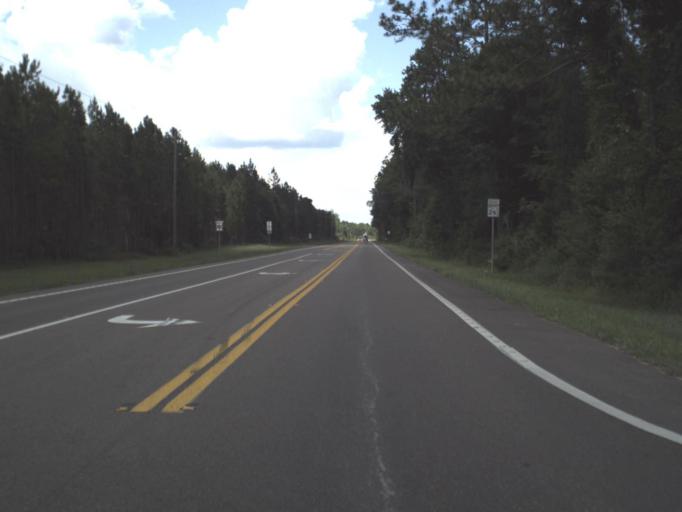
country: US
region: Florida
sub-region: Alachua County
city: Waldo
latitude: 29.6999
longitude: -82.1807
